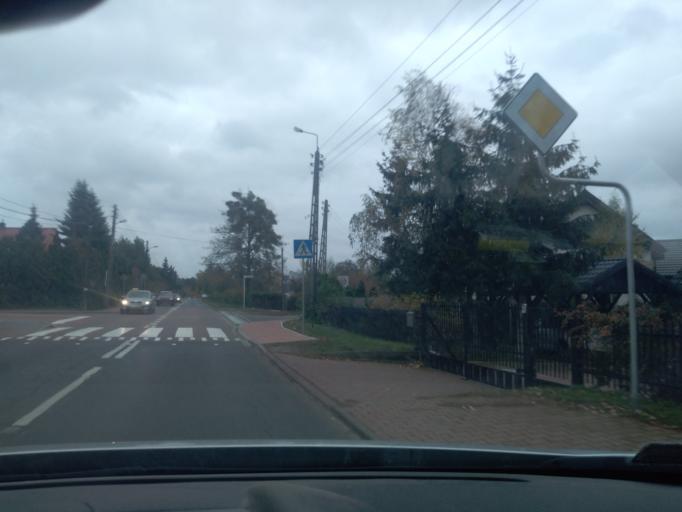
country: PL
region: Greater Poland Voivodeship
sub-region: Powiat poznanski
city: Suchy Las
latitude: 52.4749
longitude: 16.8884
